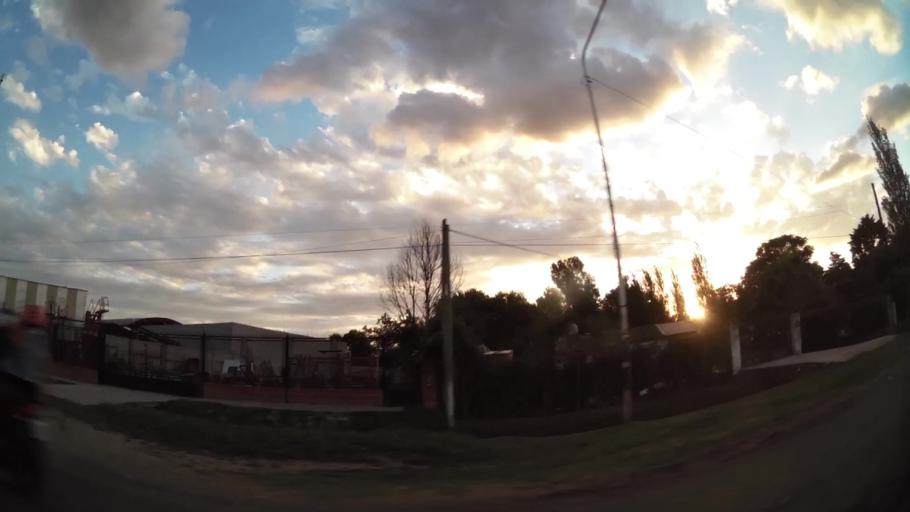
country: AR
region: Buenos Aires
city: Santa Catalina - Dique Lujan
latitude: -34.4919
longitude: -58.7660
